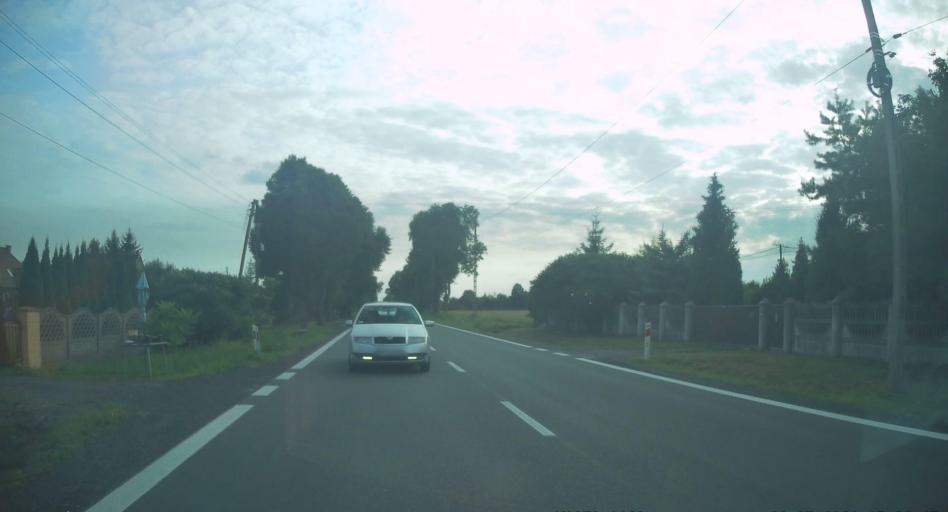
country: PL
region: Silesian Voivodeship
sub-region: Powiat czestochowski
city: Borowno
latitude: 50.9095
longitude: 19.3026
